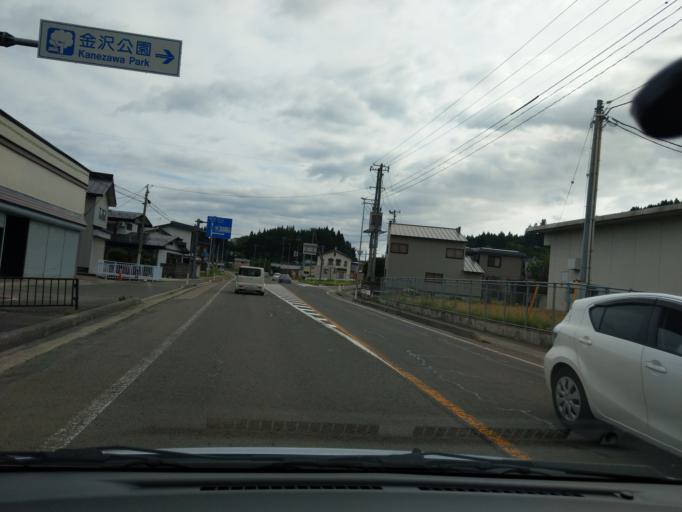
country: JP
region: Akita
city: Yokotemachi
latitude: 39.3708
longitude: 140.5688
